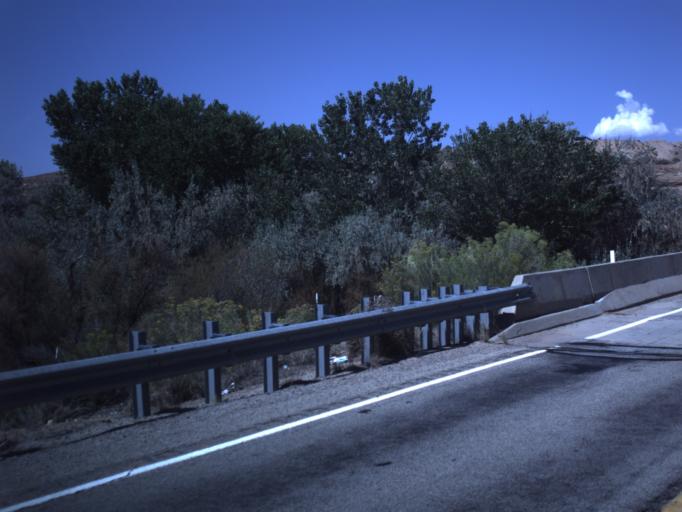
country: US
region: Utah
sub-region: San Juan County
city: Blanding
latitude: 37.2570
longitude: -109.6179
